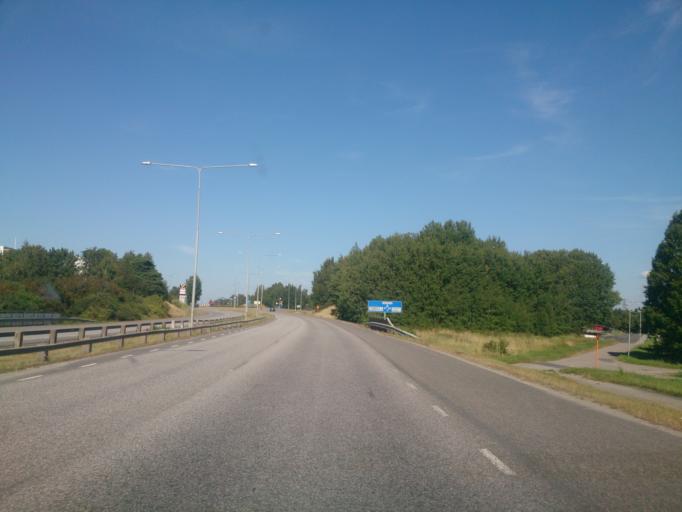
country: SE
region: OEstergoetland
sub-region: Norrkopings Kommun
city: Norrkoping
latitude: 58.5685
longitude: 16.1776
